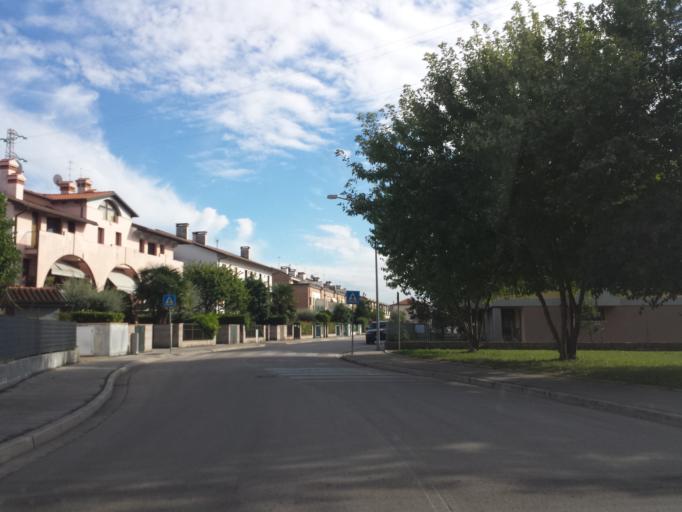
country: IT
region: Veneto
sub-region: Provincia di Vicenza
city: Villaggio Montegrappa
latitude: 45.5437
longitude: 11.5955
